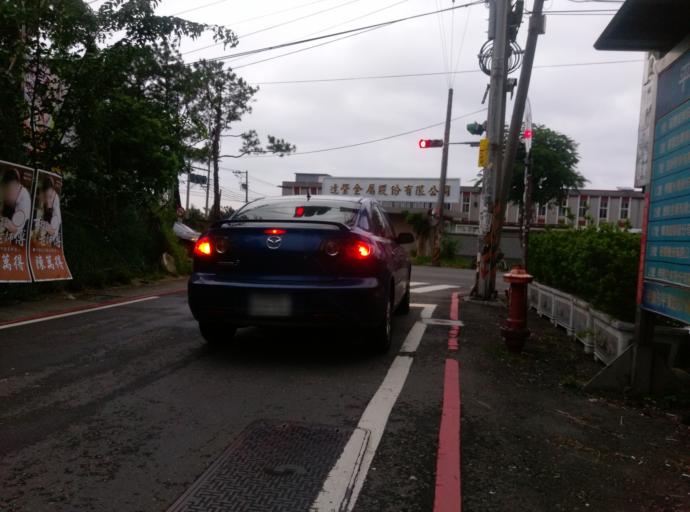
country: TW
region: Taiwan
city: Daxi
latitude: 24.9122
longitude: 121.2394
